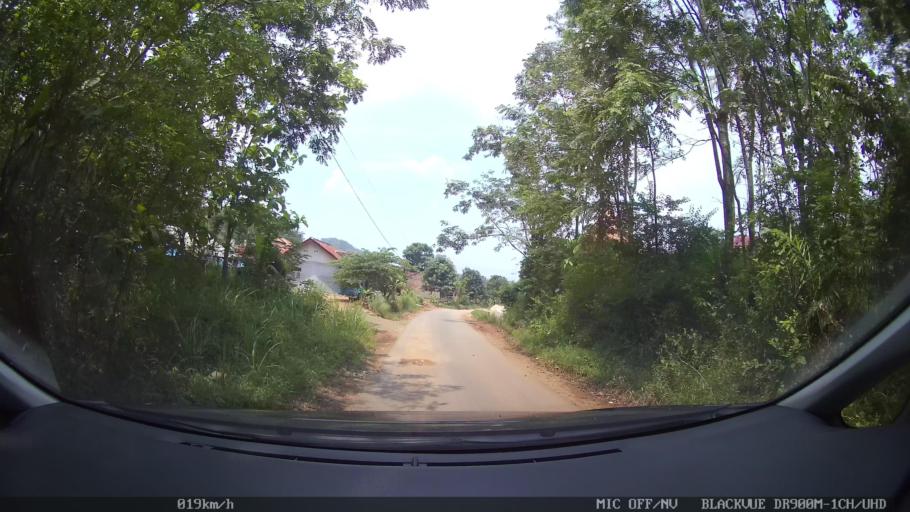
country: ID
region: Lampung
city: Pringsewu
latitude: -5.3828
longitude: 105.0106
